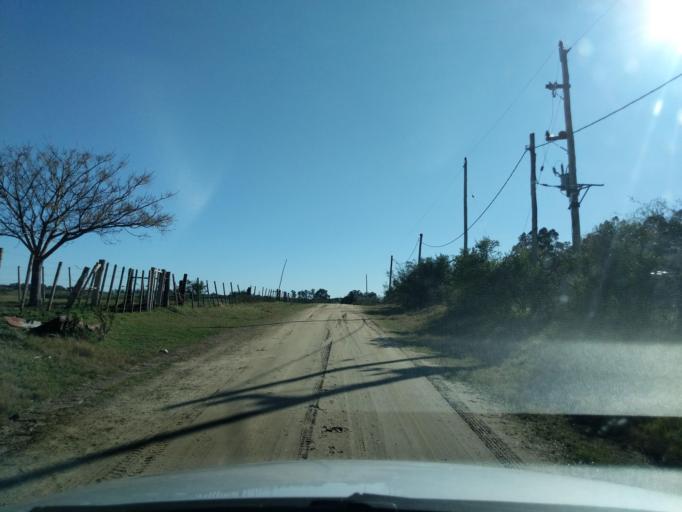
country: UY
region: Florida
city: Florida
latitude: -34.0753
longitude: -56.2678
